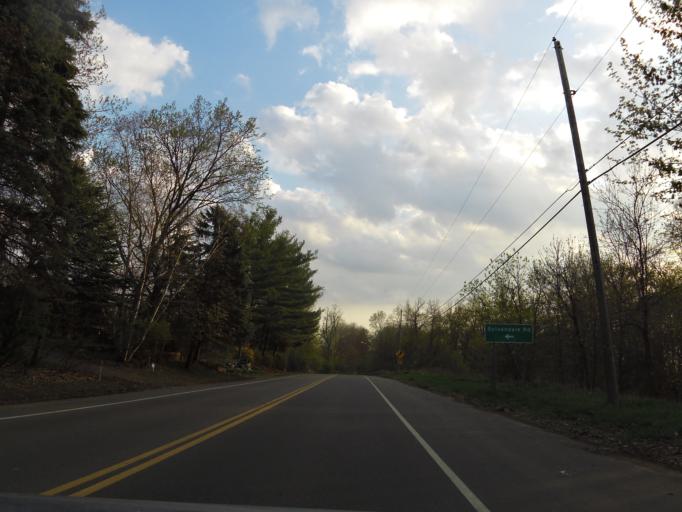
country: US
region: Minnesota
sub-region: Dakota County
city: West Saint Paul
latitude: 44.9141
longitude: -93.1164
